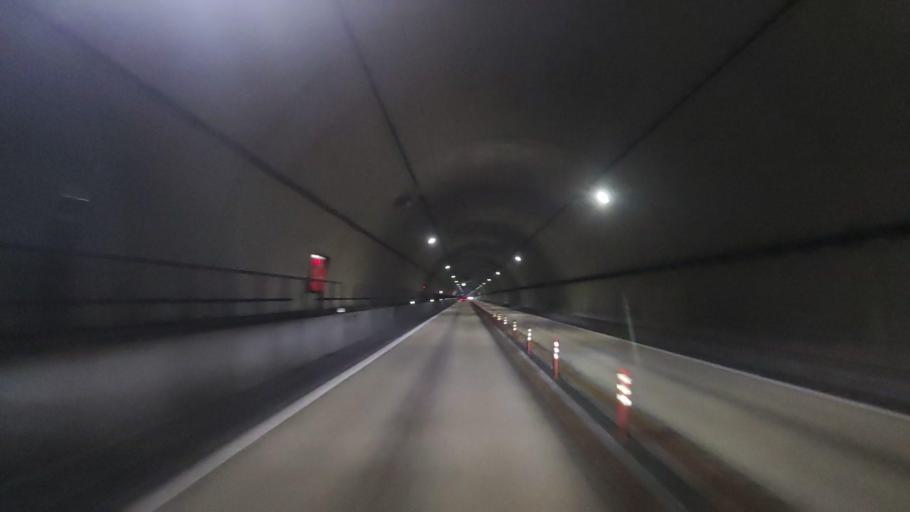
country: JP
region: Wakayama
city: Tanabe
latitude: 33.5683
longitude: 135.4887
